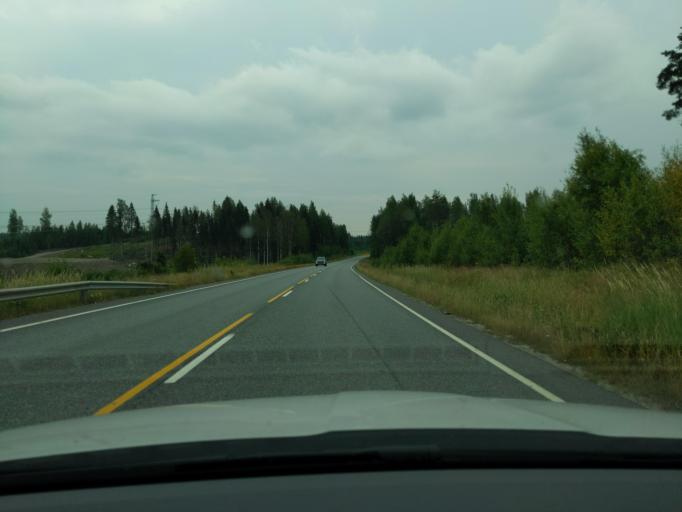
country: FI
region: Uusimaa
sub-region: Helsinki
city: Pornainen
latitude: 60.3553
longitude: 25.4049
